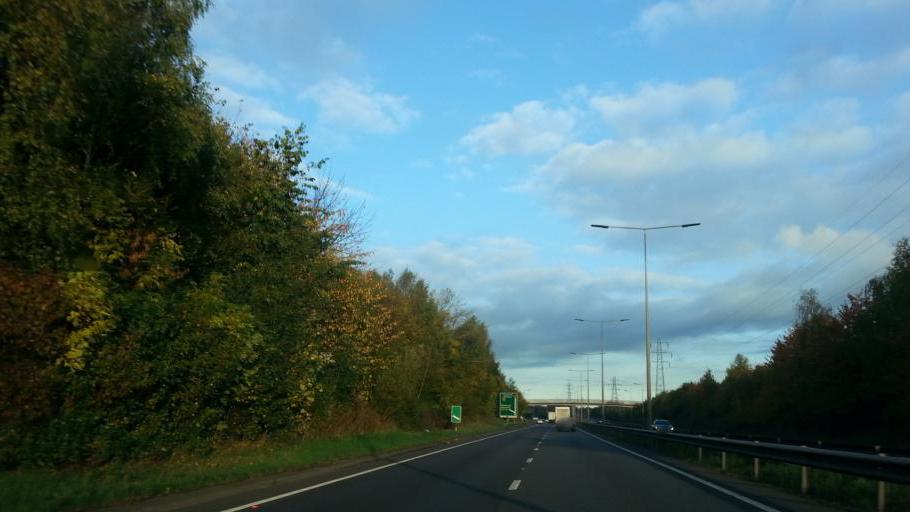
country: GB
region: England
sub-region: Staffordshire
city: Fazeley
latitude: 52.6158
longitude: -1.6649
